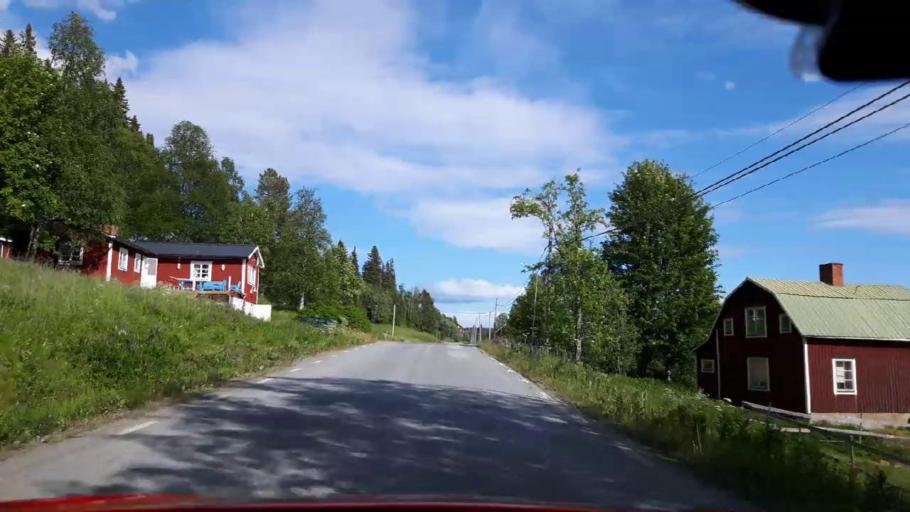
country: SE
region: Jaemtland
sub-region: Krokoms Kommun
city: Valla
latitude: 63.7687
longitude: 14.0606
